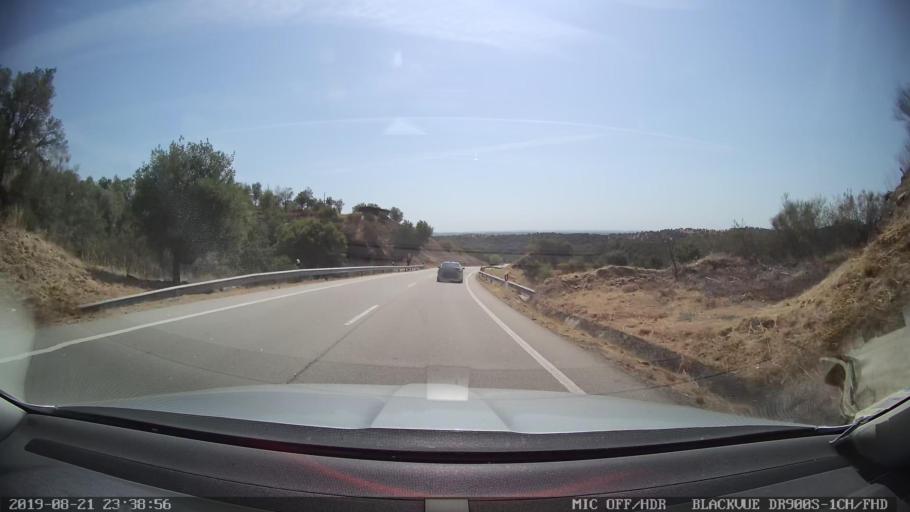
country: PT
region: Castelo Branco
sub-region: Idanha-A-Nova
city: Idanha-a-Nova
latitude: 39.8588
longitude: -7.3447
